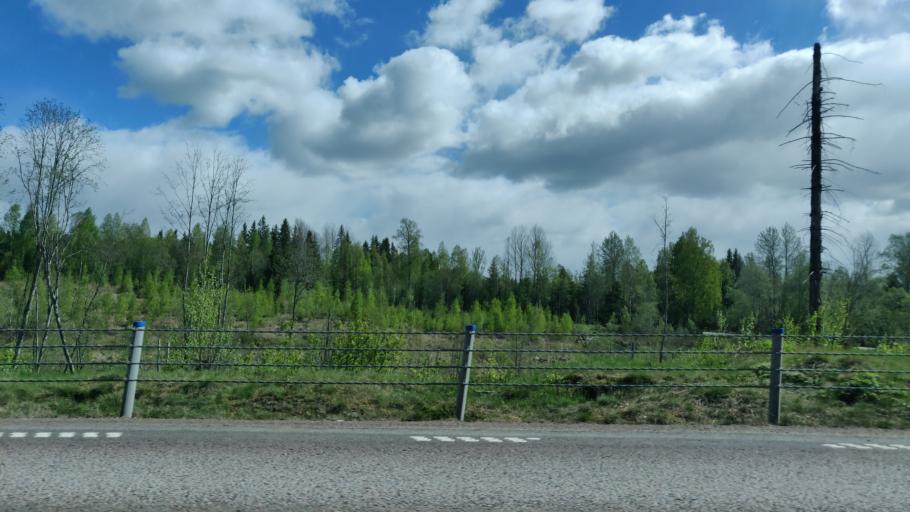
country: SE
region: Vaermland
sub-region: Karlstads Kommun
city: Molkom
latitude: 59.5594
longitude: 13.6671
